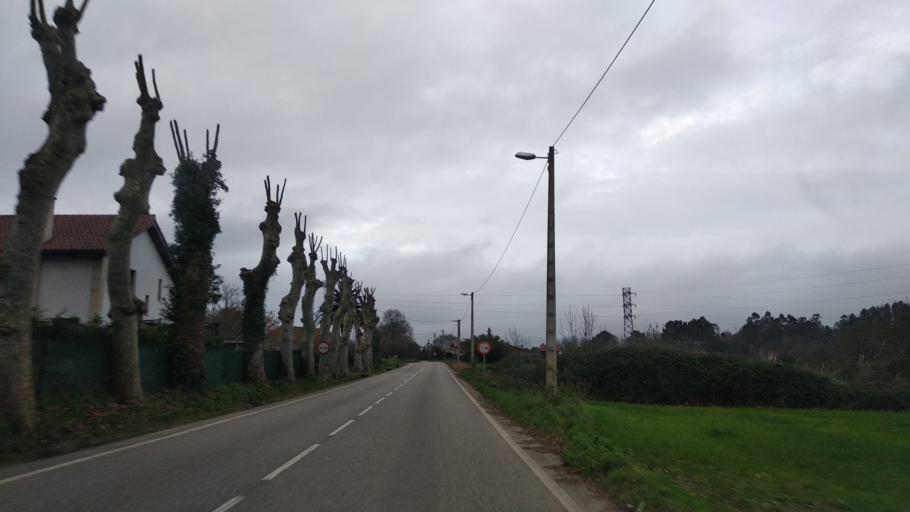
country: ES
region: Cantabria
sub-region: Provincia de Cantabria
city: Entrambasaguas
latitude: 43.4157
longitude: -3.7009
